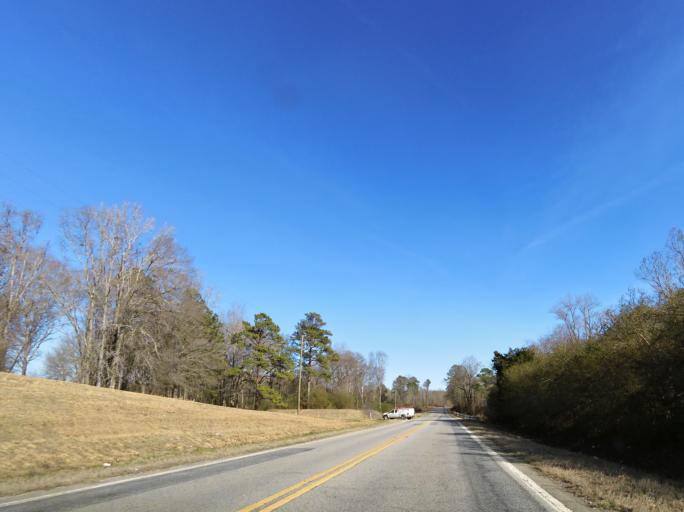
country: US
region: Georgia
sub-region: Crawford County
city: Knoxville
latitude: 32.7239
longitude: -83.9907
